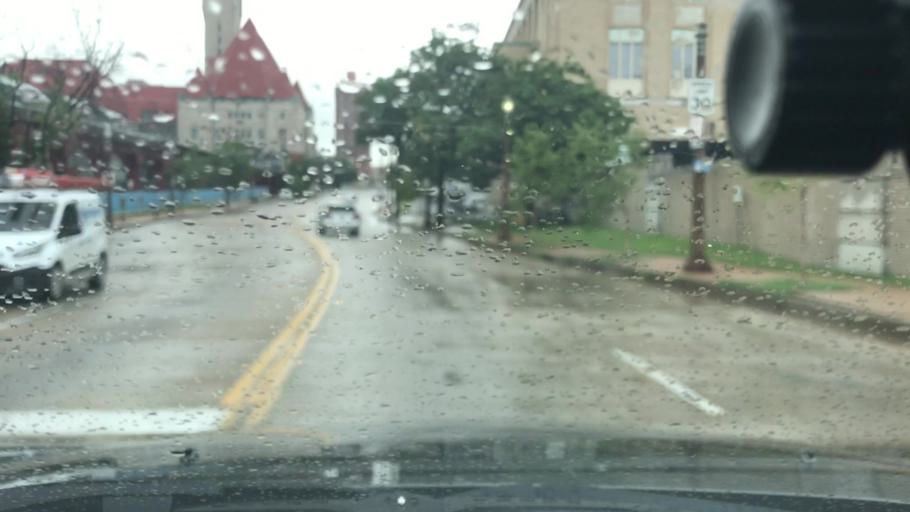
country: US
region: Missouri
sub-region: City of Saint Louis
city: St. Louis
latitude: 38.6271
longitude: -90.2069
